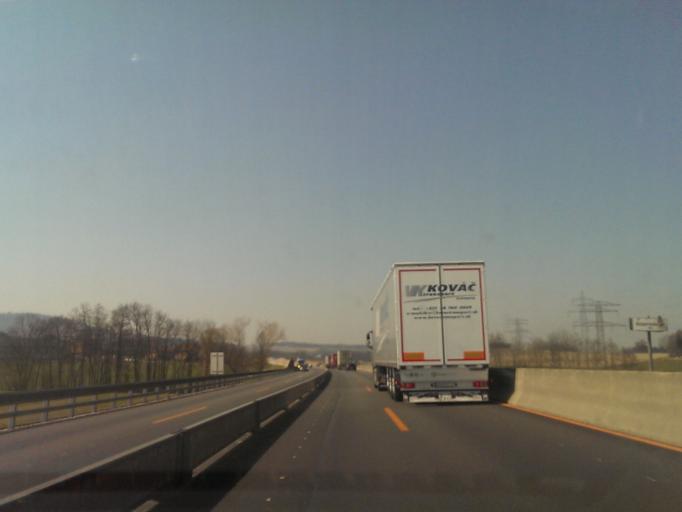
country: AT
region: Upper Austria
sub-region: Politischer Bezirk Vocklabruck
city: Wolfsegg am Hausruck
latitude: 48.1888
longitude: 13.6777
